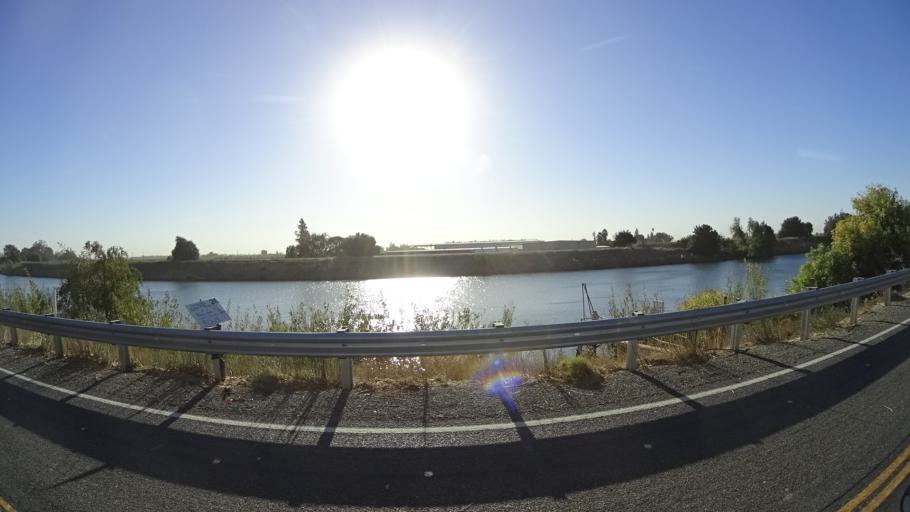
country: US
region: California
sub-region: Sacramento County
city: Walnut Grove
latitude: 38.3417
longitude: -121.5622
